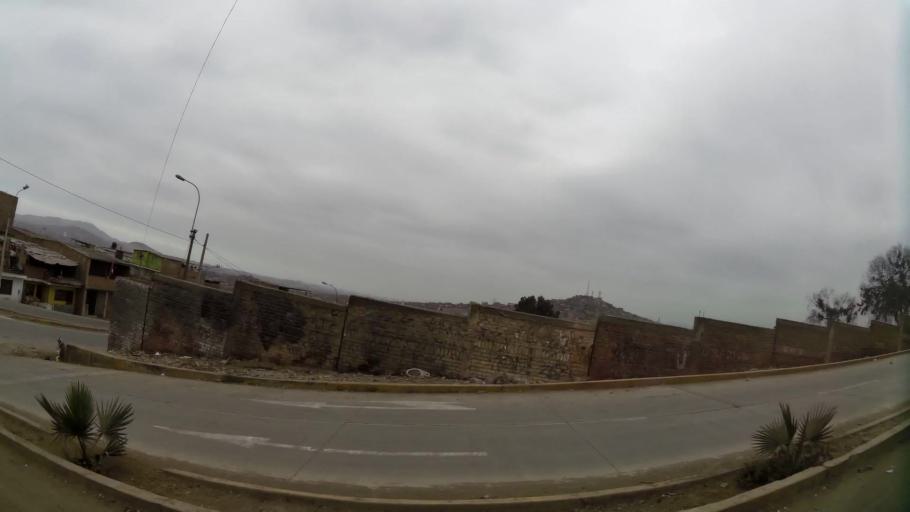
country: PE
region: Lima
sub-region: Lima
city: Surco
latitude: -12.1969
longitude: -76.9494
